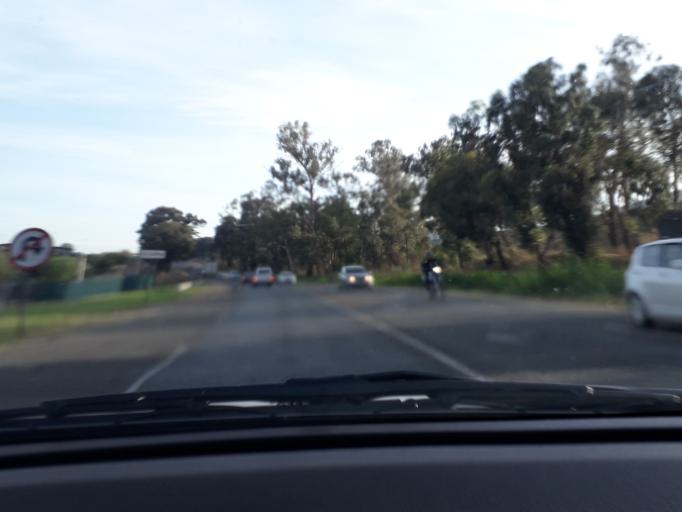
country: ZA
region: Gauteng
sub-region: City of Tshwane Metropolitan Municipality
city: Centurion
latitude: -25.9165
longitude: 28.1571
